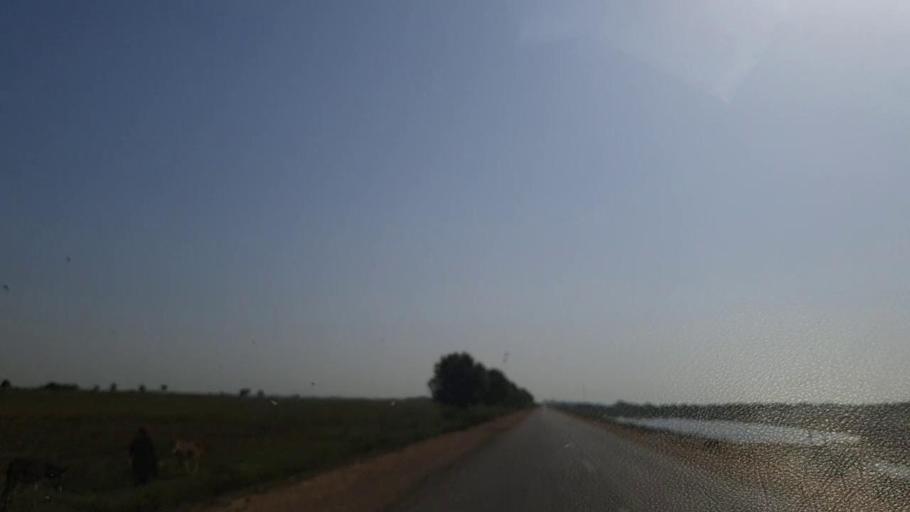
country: PK
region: Sindh
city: Jati
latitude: 24.5346
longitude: 68.2787
